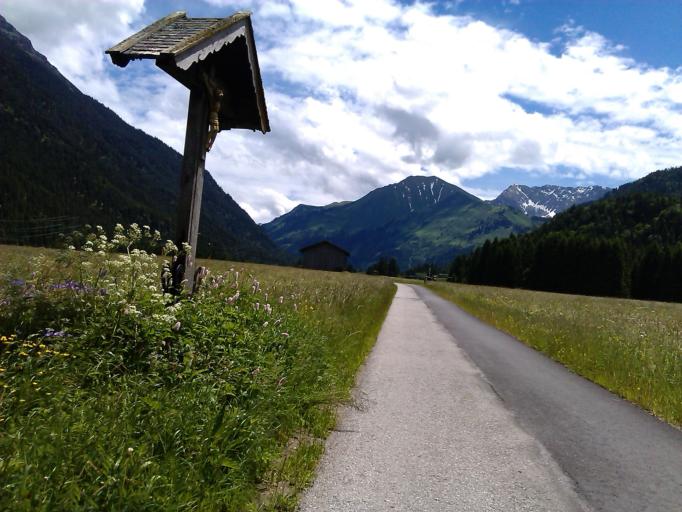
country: AT
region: Tyrol
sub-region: Politischer Bezirk Reutte
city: Heiterwang
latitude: 47.4413
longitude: 10.7547
